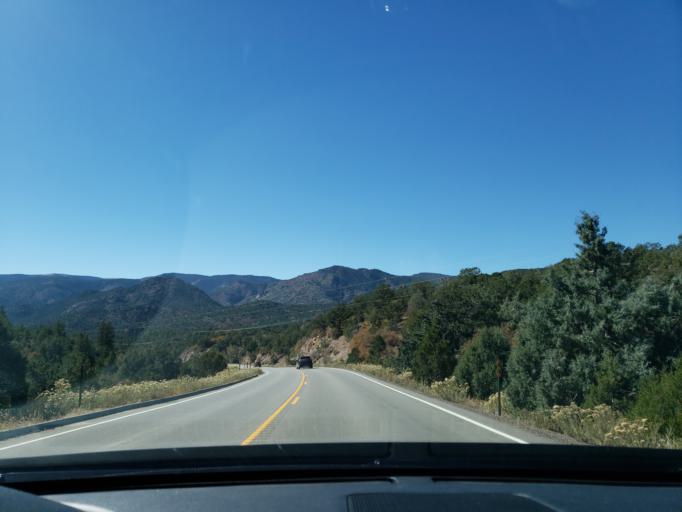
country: US
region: Colorado
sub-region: Fremont County
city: Canon City
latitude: 38.5789
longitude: -105.4202
